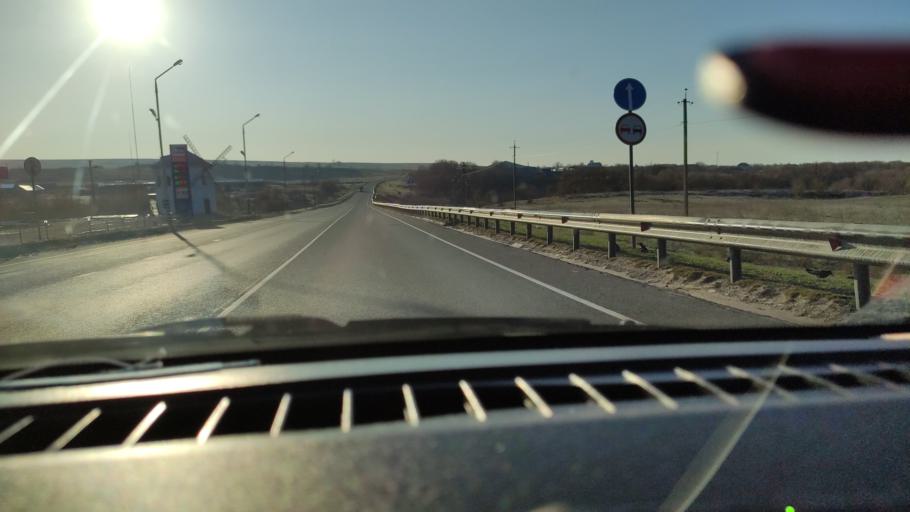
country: RU
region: Saratov
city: Tersa
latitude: 52.0983
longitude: 47.5269
